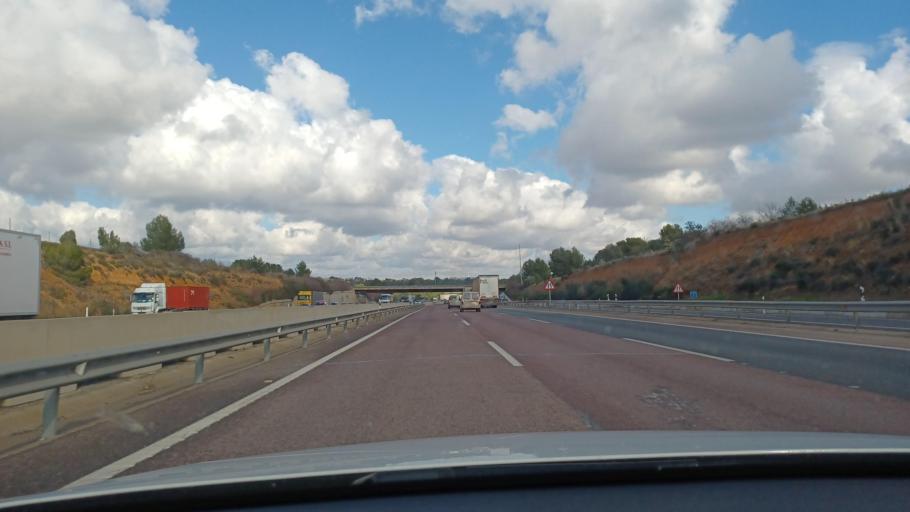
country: ES
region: Valencia
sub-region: Provincia de Valencia
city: Manises
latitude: 39.5193
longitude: -0.4768
